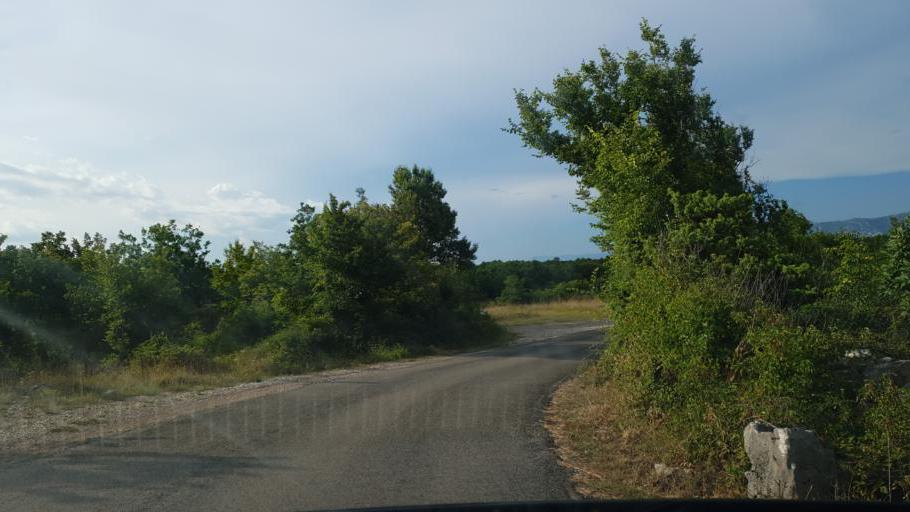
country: HR
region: Primorsko-Goranska
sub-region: Grad Crikvenica
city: Jadranovo
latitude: 45.1700
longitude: 14.6063
